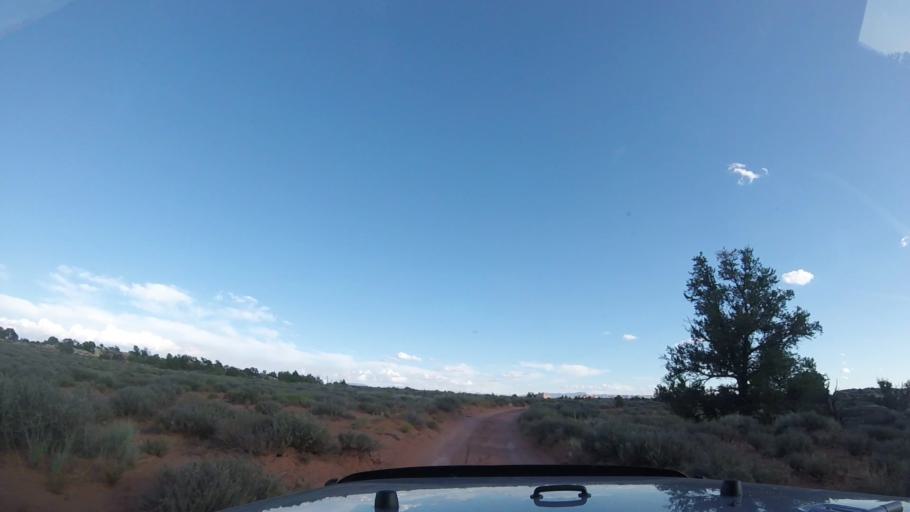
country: US
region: Utah
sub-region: Grand County
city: Moab
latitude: 38.2020
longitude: -109.7831
